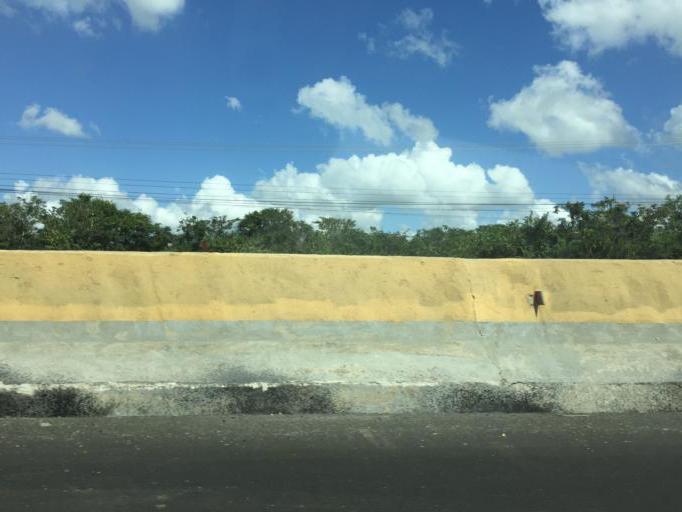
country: DO
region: Santo Domingo
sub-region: Santo Domingo
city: Santo Domingo Este
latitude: 18.4643
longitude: -69.7612
